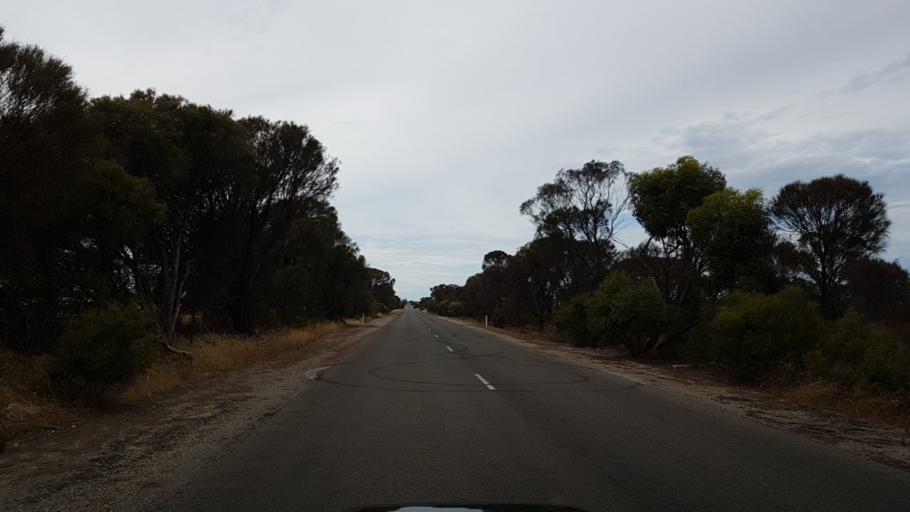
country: AU
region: South Australia
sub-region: Yorke Peninsula
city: Port Victoria
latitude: -34.9329
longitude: 137.0882
